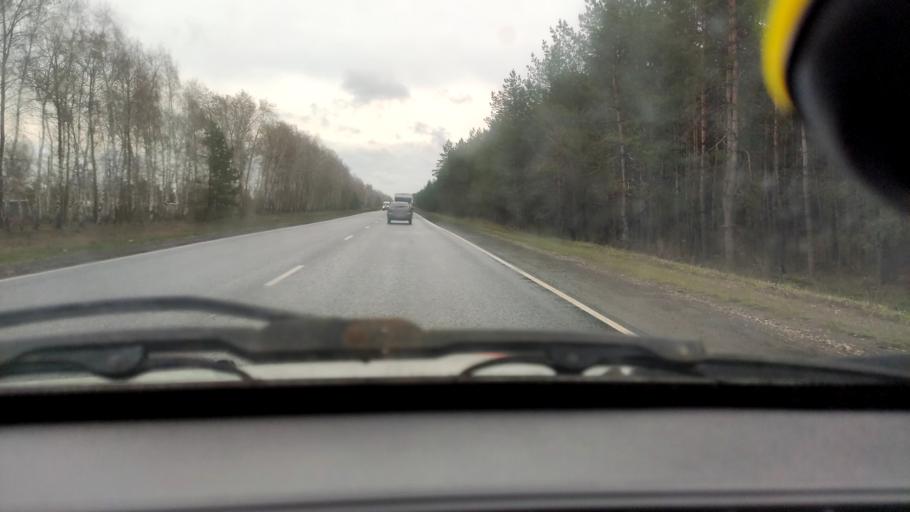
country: RU
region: Samara
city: Povolzhskiy
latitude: 53.6134
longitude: 49.6237
